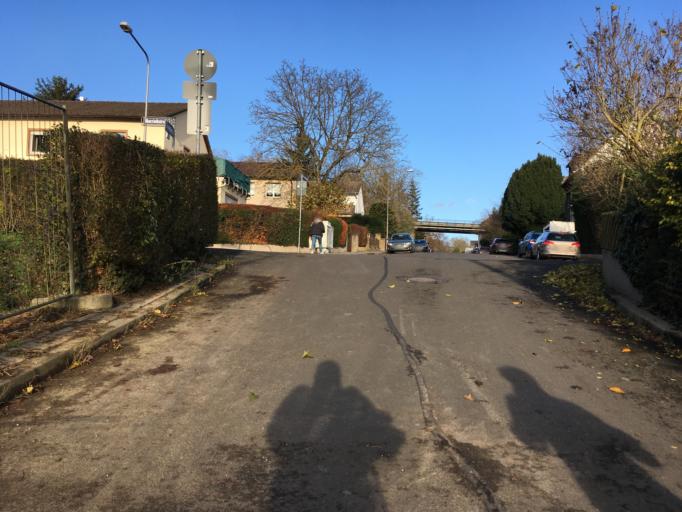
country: DE
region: Hesse
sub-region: Regierungsbezirk Darmstadt
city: Wiesbaden
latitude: 50.0608
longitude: 8.2283
